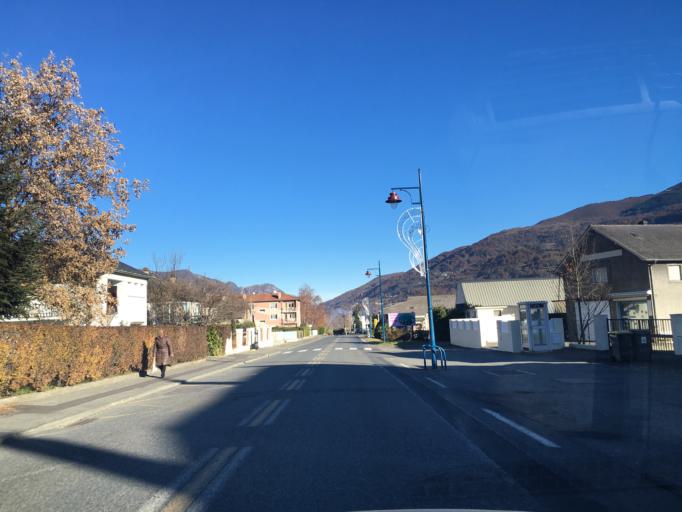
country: FR
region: Midi-Pyrenees
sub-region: Departement des Hautes-Pyrenees
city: Pierrefitte-Nestalas
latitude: 42.9644
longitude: -0.0742
